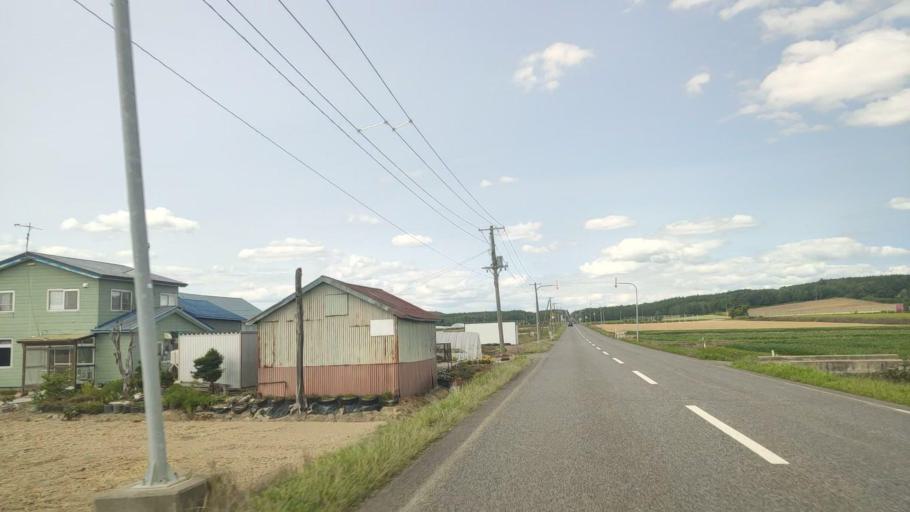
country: JP
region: Hokkaido
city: Nayoro
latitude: 44.2320
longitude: 142.4157
